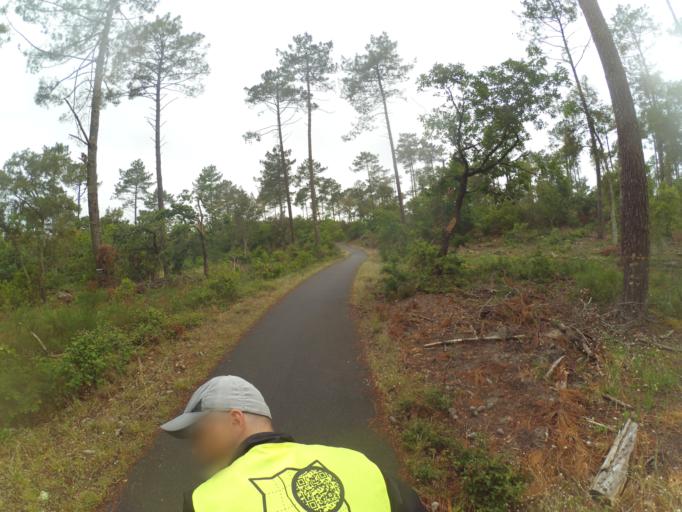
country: FR
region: Aquitaine
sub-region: Departement des Landes
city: Mimizan
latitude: 44.2187
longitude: -1.2475
